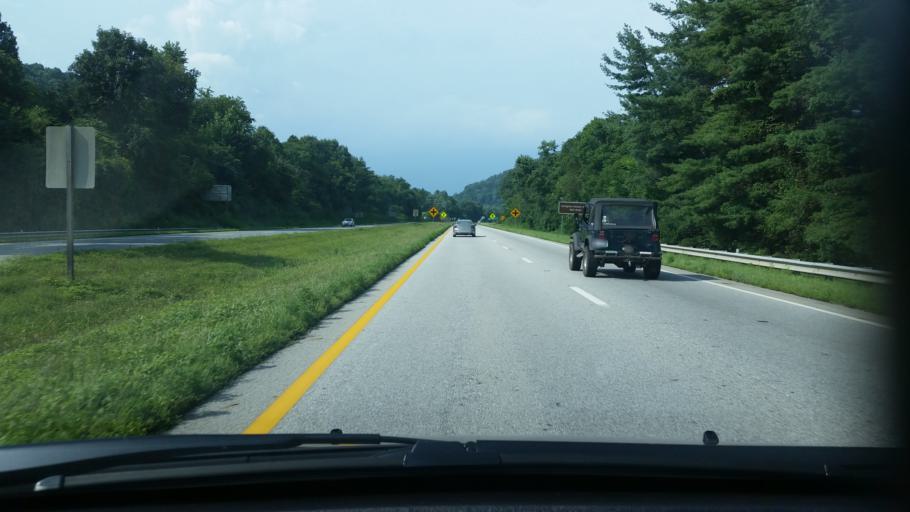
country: US
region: Virginia
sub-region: Nelson County
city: Lovingston
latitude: 37.7566
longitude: -78.8747
